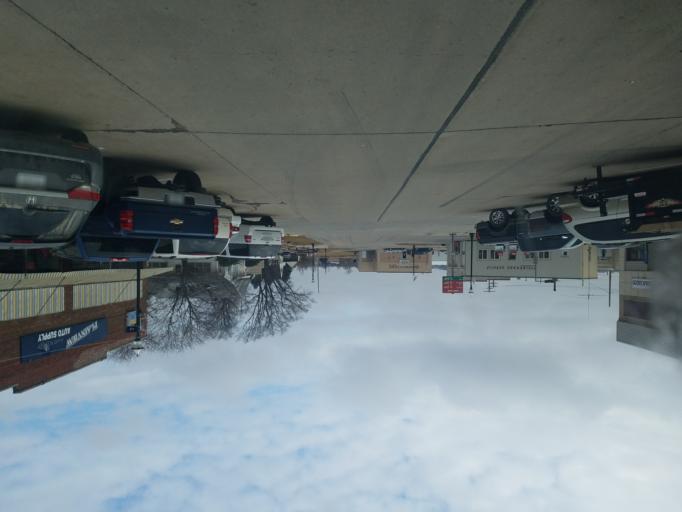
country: US
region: Nebraska
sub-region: Pierce County
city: Plainview
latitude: 42.3496
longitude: -97.7943
